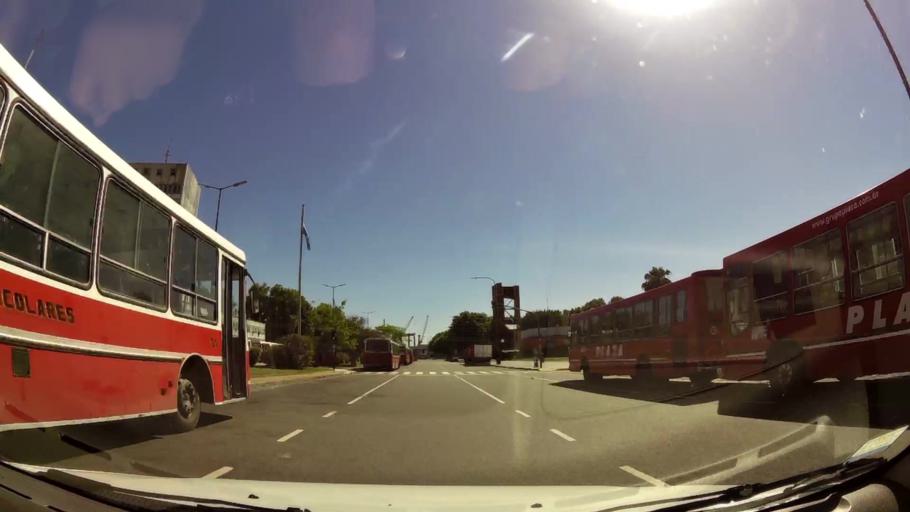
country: AR
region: Buenos Aires F.D.
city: Retiro
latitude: -34.5856
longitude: -58.3700
